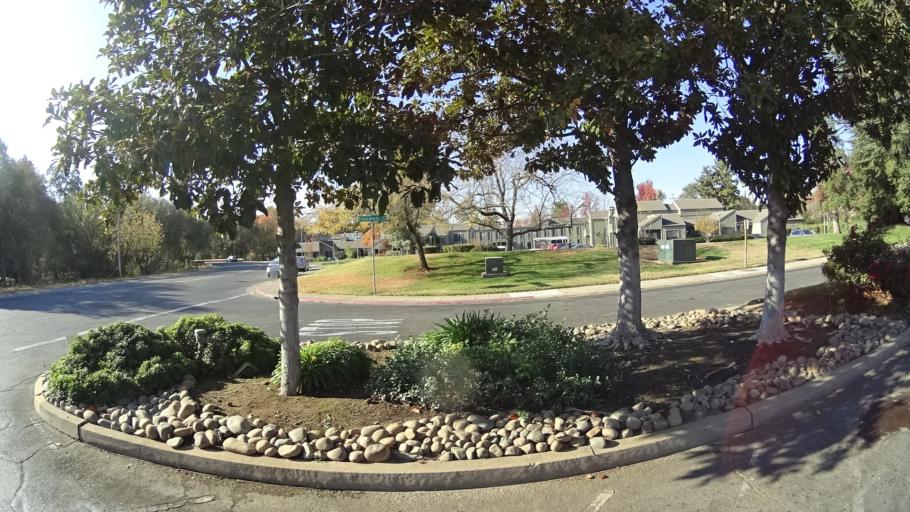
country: US
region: California
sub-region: Sacramento County
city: Citrus Heights
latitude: 38.6885
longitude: -121.3049
